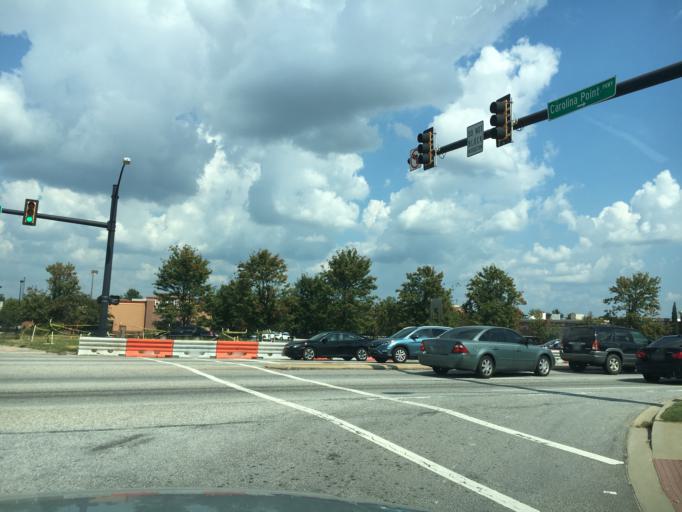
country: US
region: South Carolina
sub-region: Greenville County
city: Mauldin
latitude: 34.8276
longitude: -82.3011
